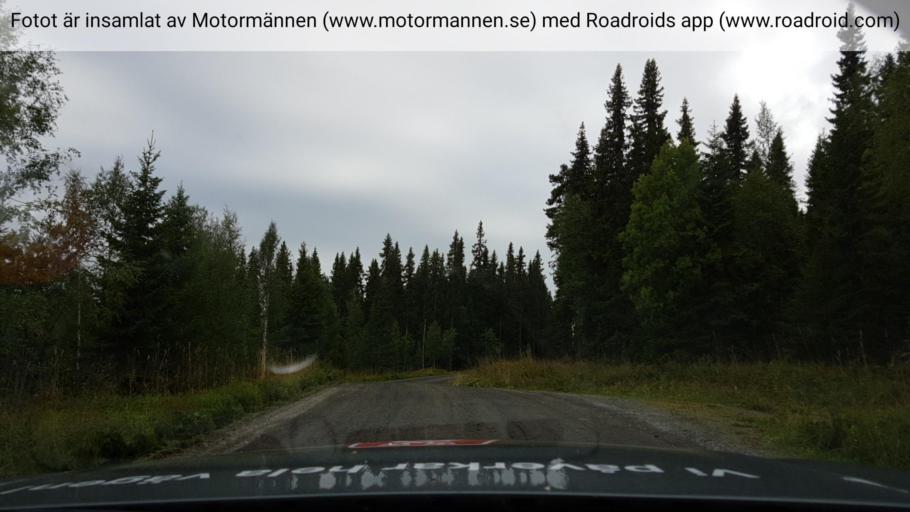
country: SE
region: Jaemtland
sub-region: Krokoms Kommun
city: Valla
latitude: 63.3930
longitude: 14.0633
